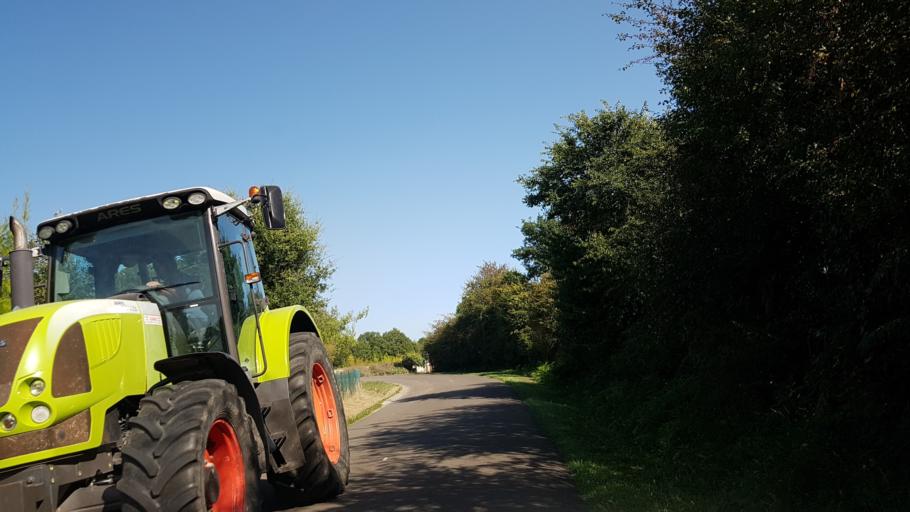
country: FR
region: Poitou-Charentes
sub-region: Departement de la Charente-Maritime
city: Breuillet
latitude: 45.7017
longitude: -1.0506
